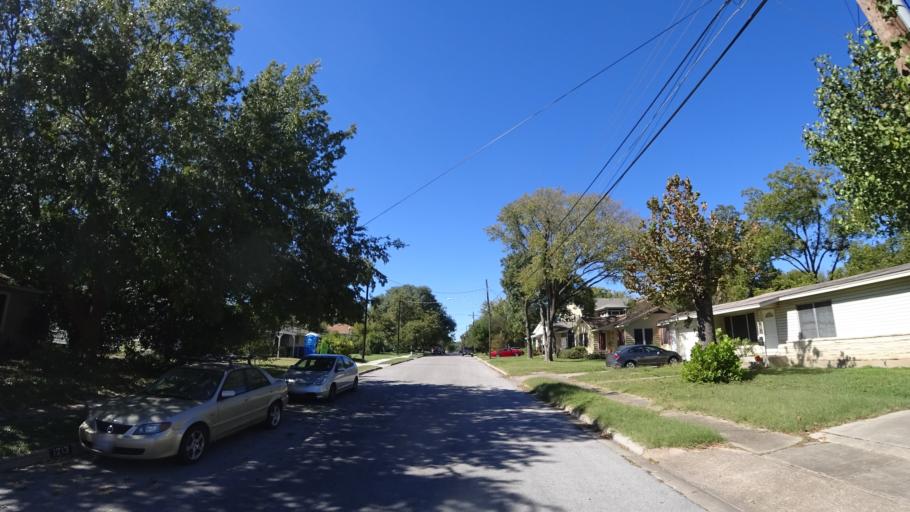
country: US
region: Texas
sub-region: Travis County
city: Austin
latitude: 30.3348
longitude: -97.7272
